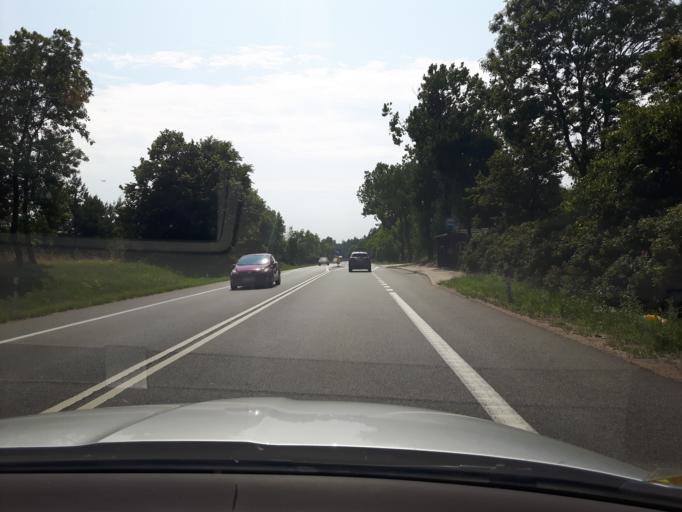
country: PL
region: Masovian Voivodeship
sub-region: Powiat mlawski
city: Mlawa
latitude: 53.1490
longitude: 20.4035
